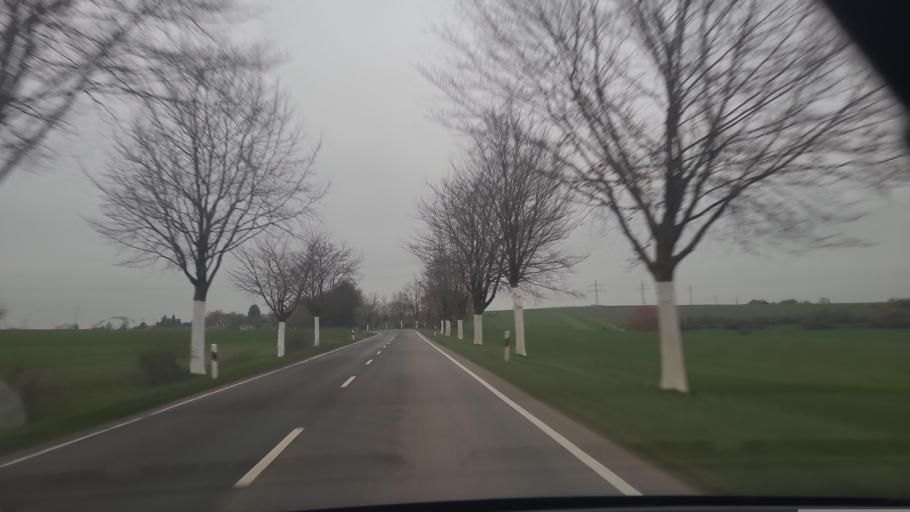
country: LU
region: Luxembourg
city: Schouweiler
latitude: 49.5933
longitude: 5.9595
